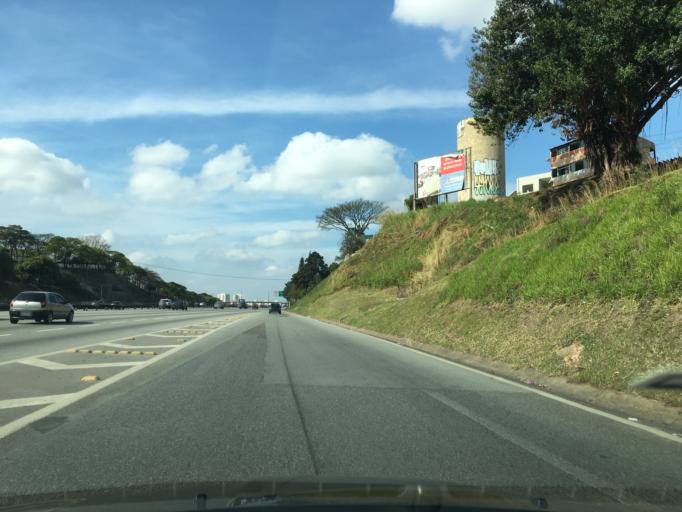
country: BR
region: Sao Paulo
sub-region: Guarulhos
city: Guarulhos
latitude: -23.4972
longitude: -46.5572
